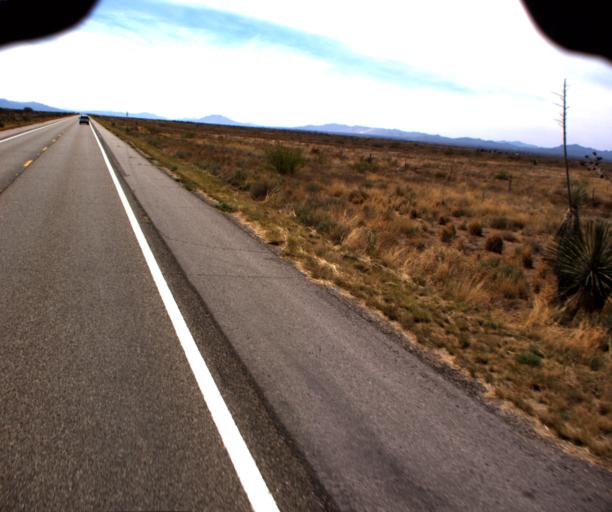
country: US
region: Arizona
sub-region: Cochise County
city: Pirtleville
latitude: 31.5180
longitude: -109.6447
